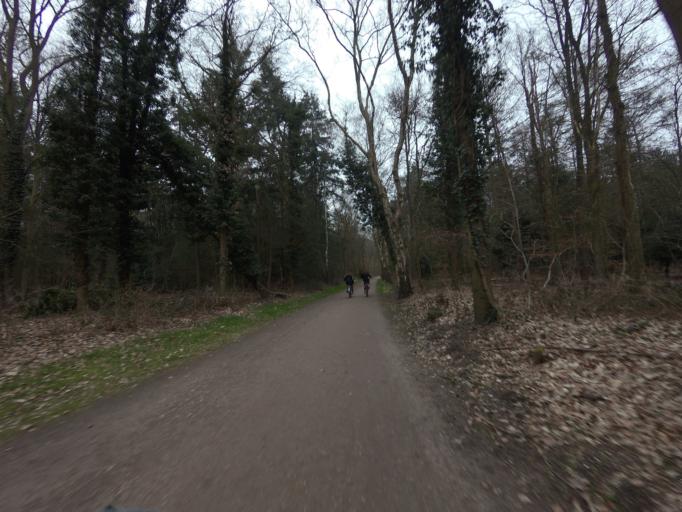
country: NL
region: North Holland
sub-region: Gemeente Hilversum
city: Hilversum
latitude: 52.2283
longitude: 5.1514
